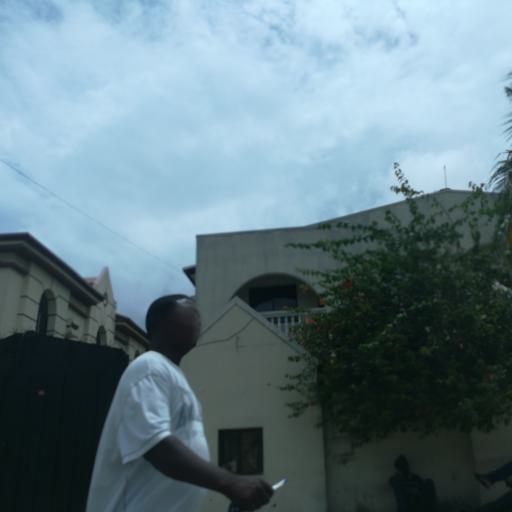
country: NG
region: Lagos
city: Ikoyi
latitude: 6.4457
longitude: 3.4615
